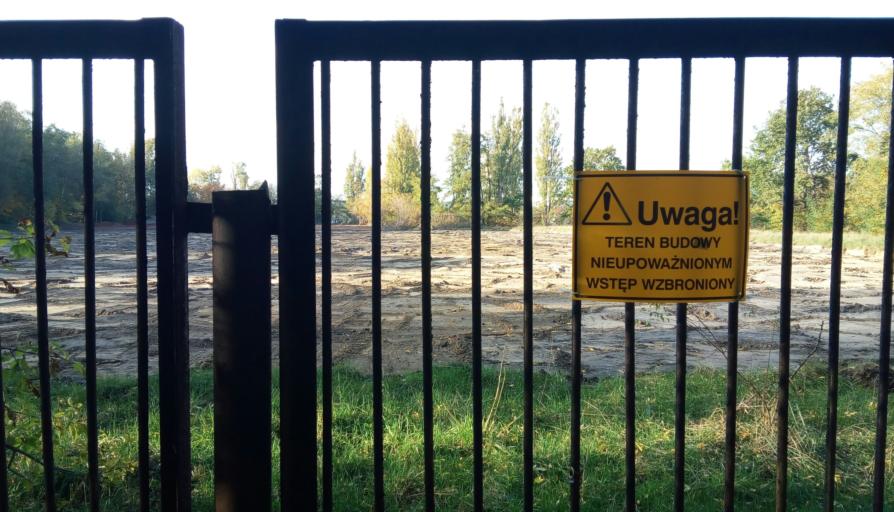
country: PL
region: Masovian Voivodeship
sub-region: Warszawa
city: Bielany
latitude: 52.3004
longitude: 20.9484
